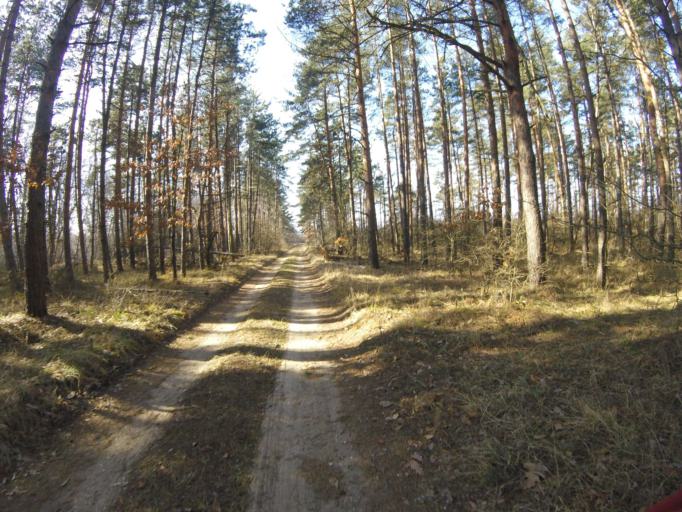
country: HU
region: Komarom-Esztergom
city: Oroszlany
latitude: 47.4615
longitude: 18.3529
